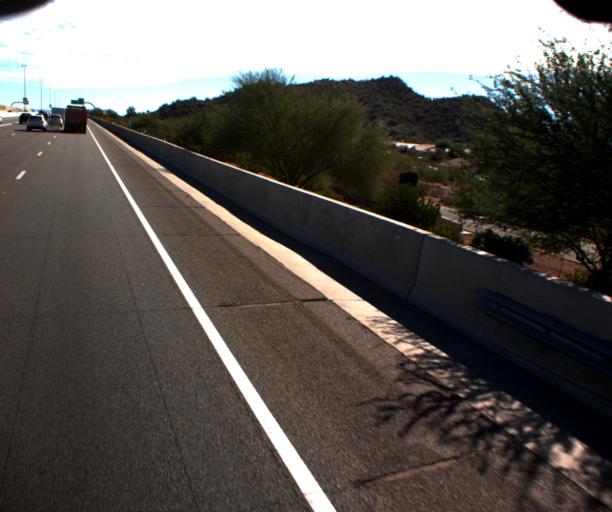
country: US
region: Arizona
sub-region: Maricopa County
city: Paradise Valley
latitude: 33.6689
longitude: -112.0523
